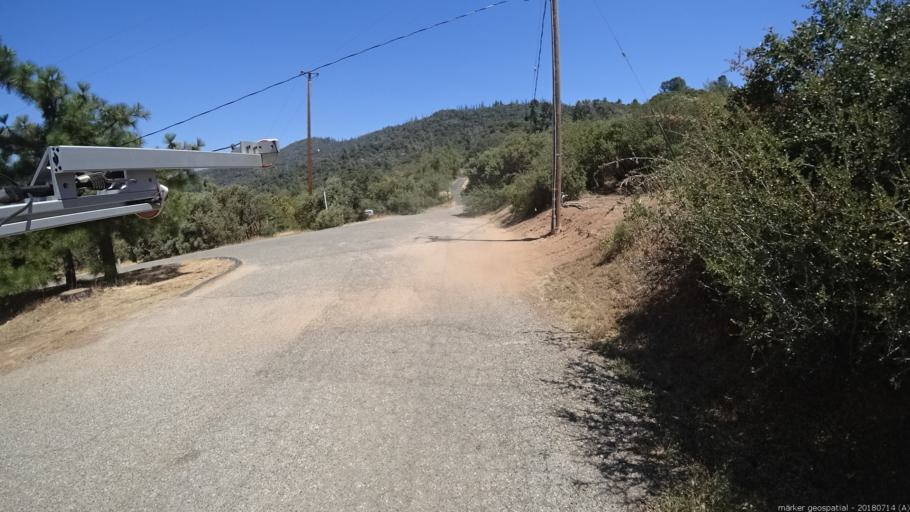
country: US
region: California
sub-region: Madera County
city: Ahwahnee
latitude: 37.4076
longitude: -119.7043
